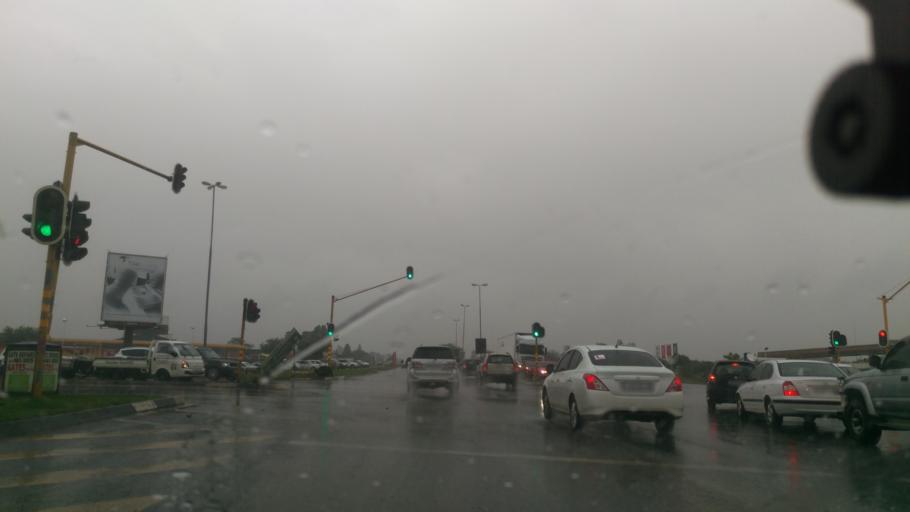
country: ZA
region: Gauteng
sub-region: West Rand District Municipality
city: Muldersdriseloop
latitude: -26.0436
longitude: 27.9555
